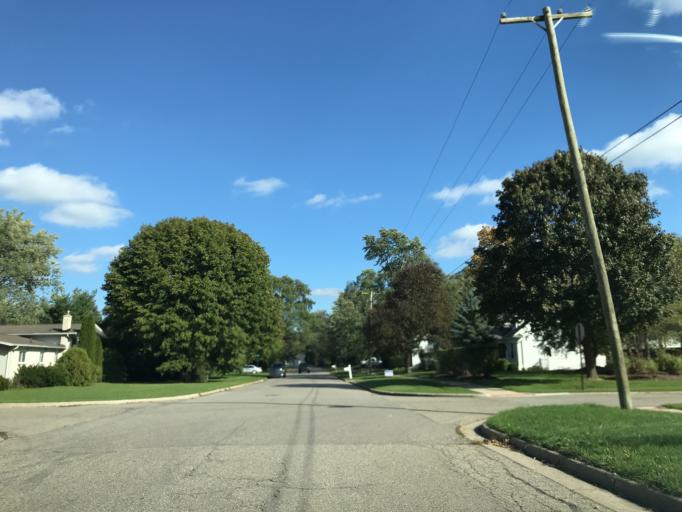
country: US
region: Michigan
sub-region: Washtenaw County
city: Ypsilanti
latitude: 42.2494
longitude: -83.6693
